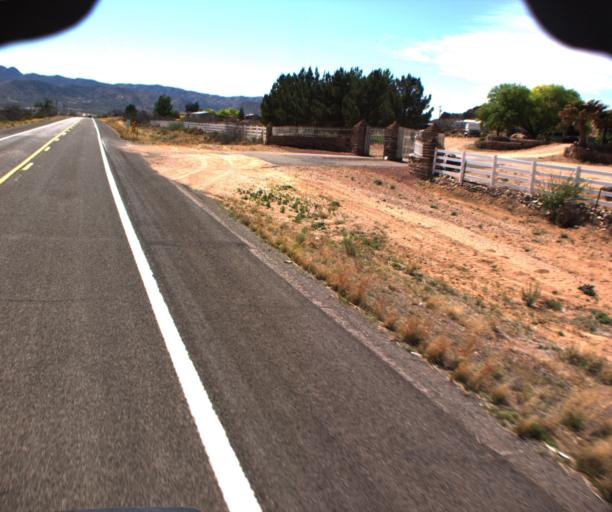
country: US
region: Arizona
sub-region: Mohave County
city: Peach Springs
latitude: 35.3667
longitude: -113.6752
